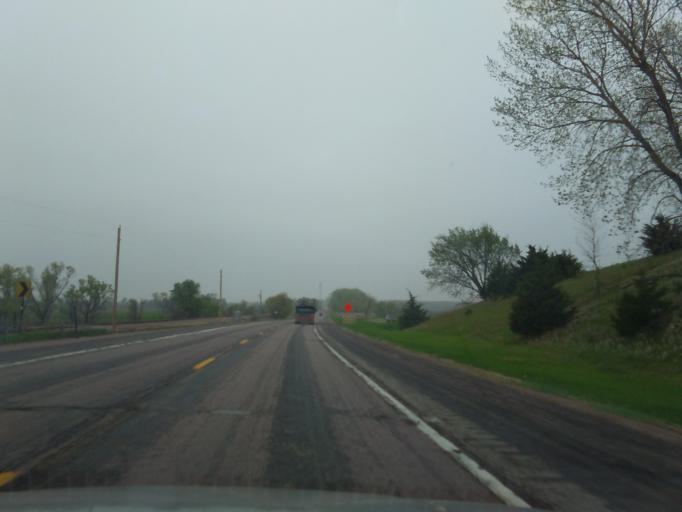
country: US
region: Nebraska
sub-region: Burt County
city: Oakland
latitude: 41.8018
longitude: -96.4814
